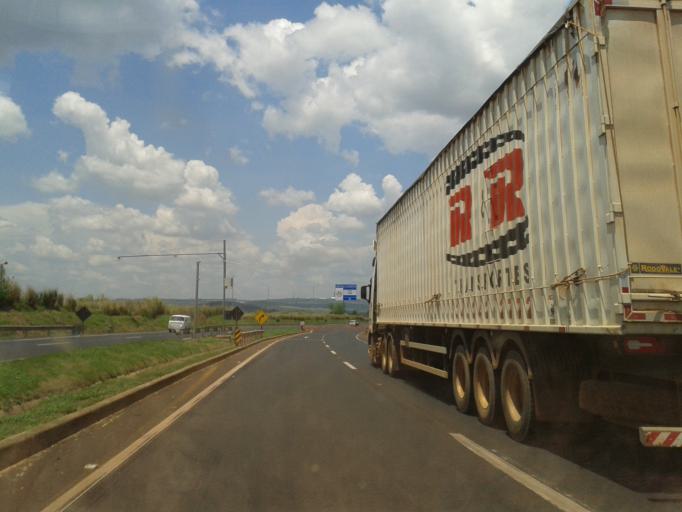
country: BR
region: Minas Gerais
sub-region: Araguari
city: Araguari
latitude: -18.7468
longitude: -48.2328
